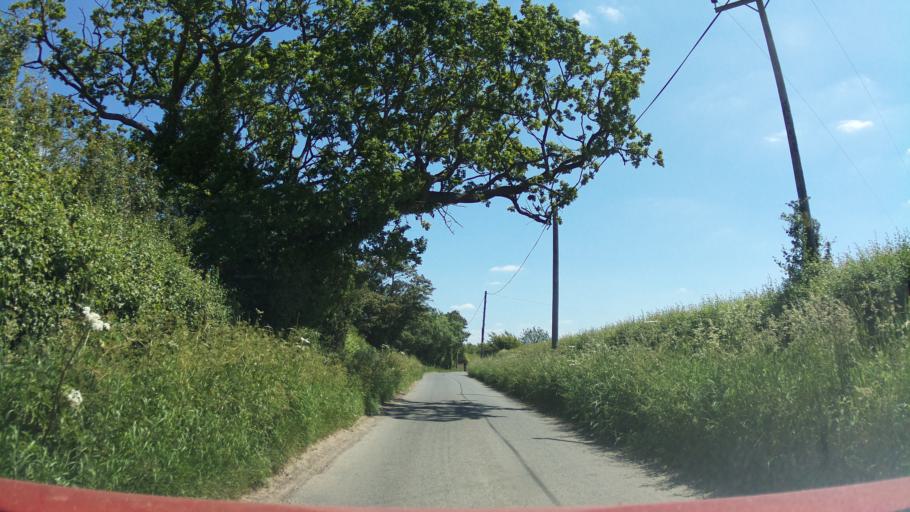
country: GB
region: England
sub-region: Wiltshire
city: Bremhill
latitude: 51.4638
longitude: -2.0707
